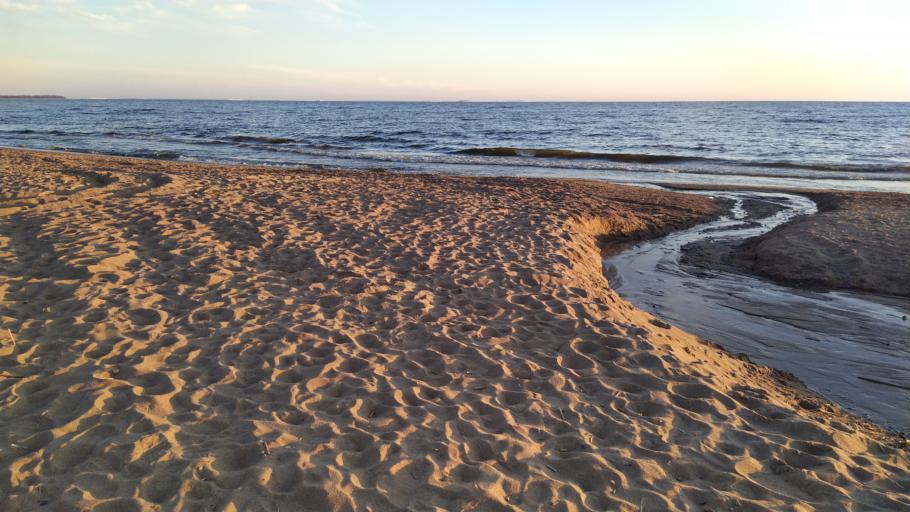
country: RU
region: St.-Petersburg
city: Solnechnoye
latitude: 60.1452
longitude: 29.9254
